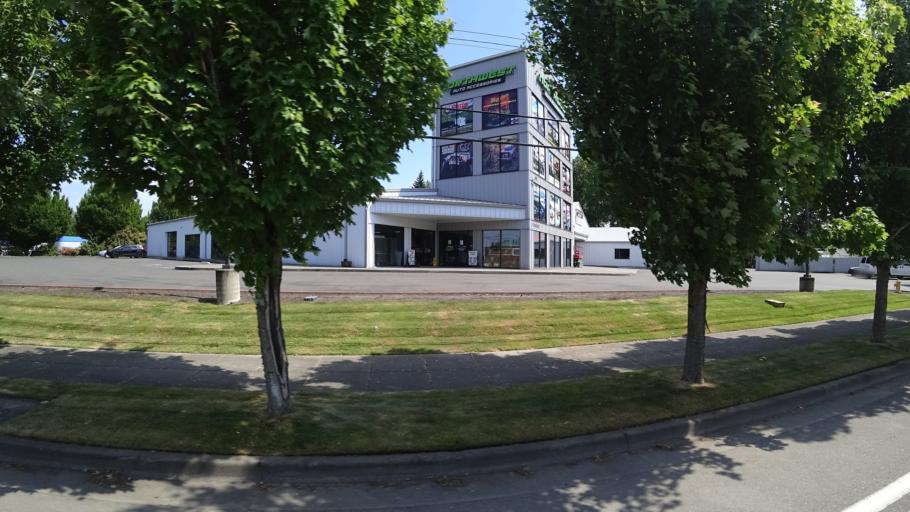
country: US
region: Oregon
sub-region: Multnomah County
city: Lents
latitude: 45.5674
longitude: -122.5532
